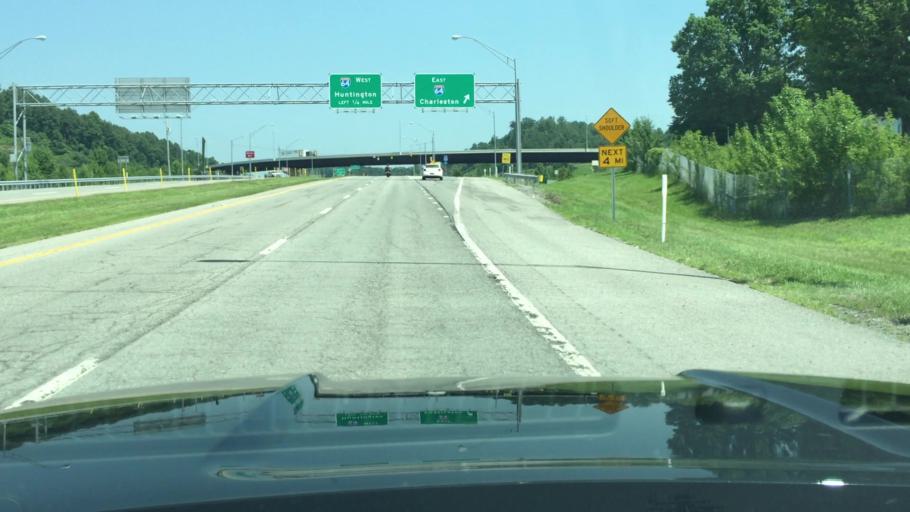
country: US
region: West Virginia
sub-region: Putnam County
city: Teays Valley
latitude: 38.4507
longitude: -81.9029
